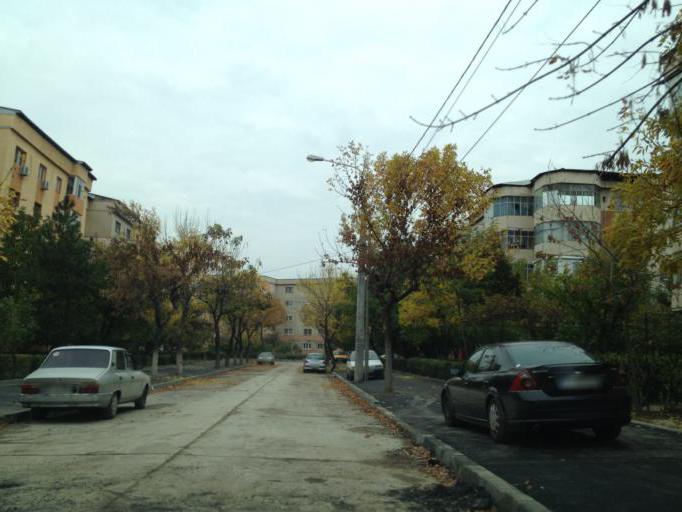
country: RO
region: Dolj
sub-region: Municipiul Craiova
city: Popoveni
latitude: 44.2985
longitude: 23.7914
